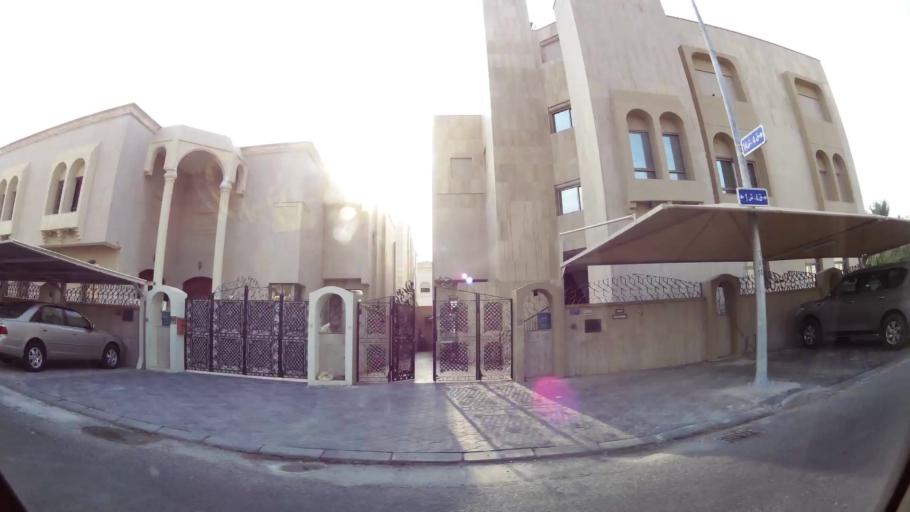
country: KW
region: Muhafazat Hawalli
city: Hawalli
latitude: 29.3096
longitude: 47.9998
